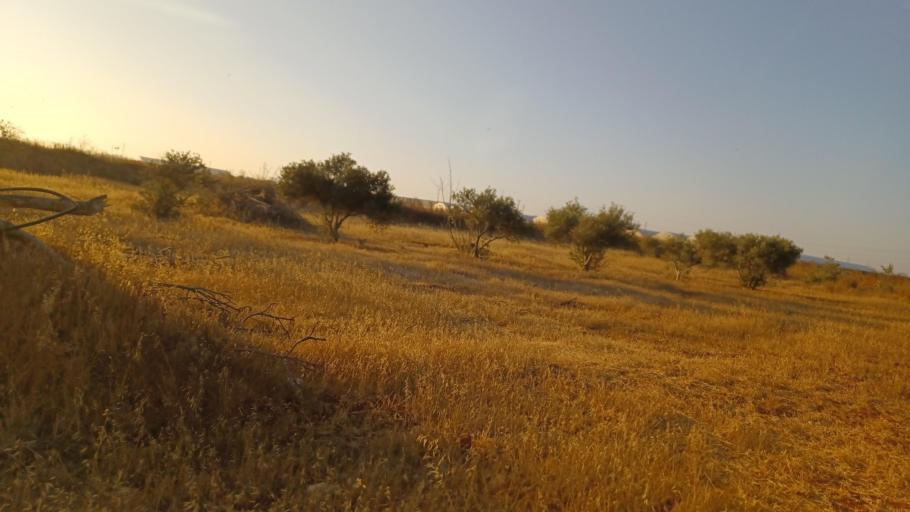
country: CY
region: Ammochostos
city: Avgorou
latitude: 35.0113
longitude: 33.8001
